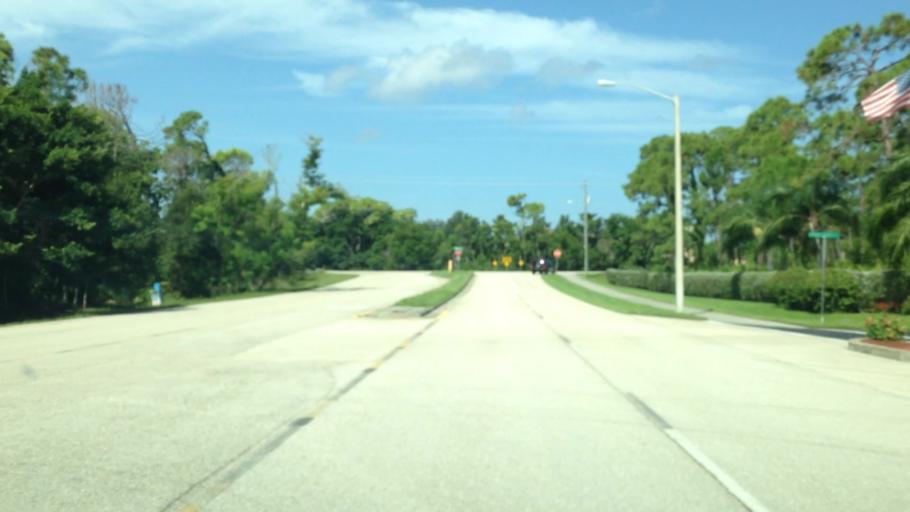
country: US
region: Florida
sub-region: Lee County
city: Bonita Springs
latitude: 26.3163
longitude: -81.8177
